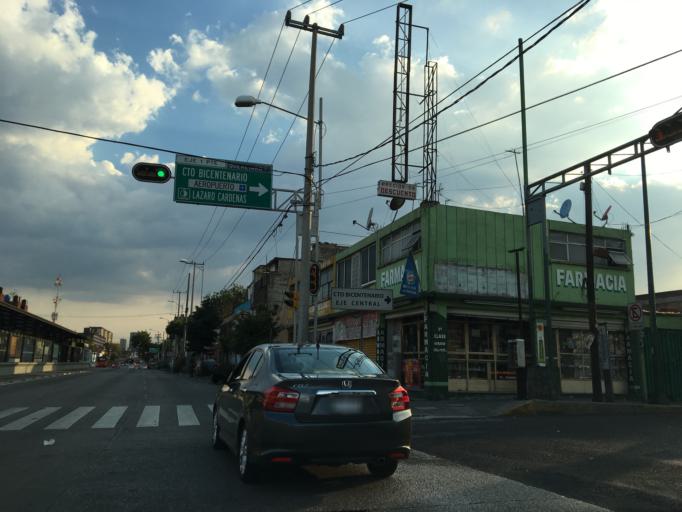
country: MX
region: Mexico City
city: Cuauhtemoc
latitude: 19.4606
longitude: -99.1440
